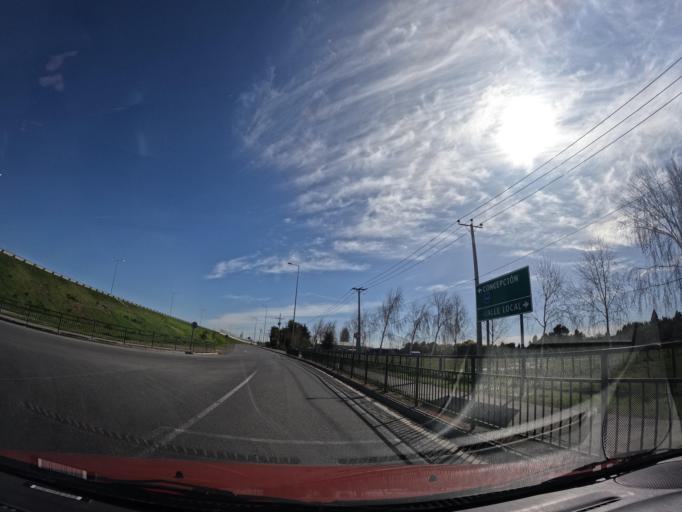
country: CL
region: Biobio
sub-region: Provincia de Biobio
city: Cabrero
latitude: -37.0301
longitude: -72.4292
